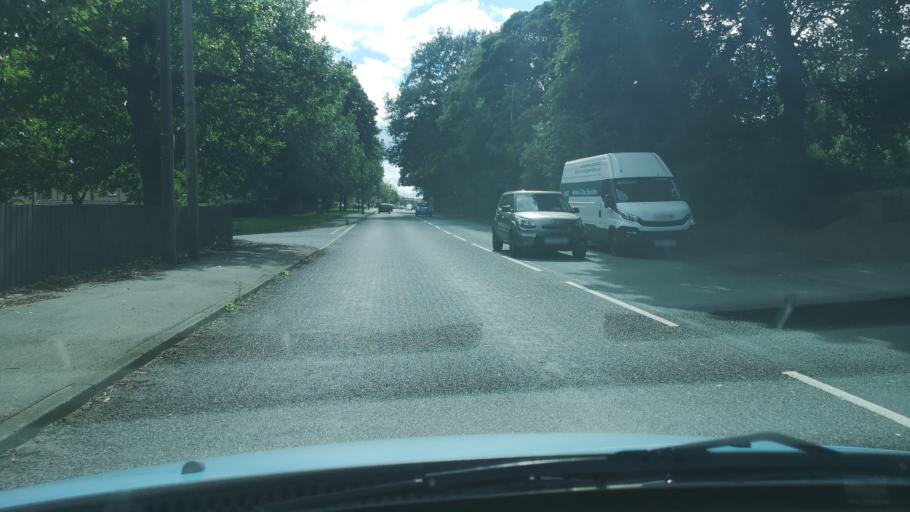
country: GB
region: England
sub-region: Kirklees
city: Liversedge
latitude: 53.7032
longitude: -1.6952
